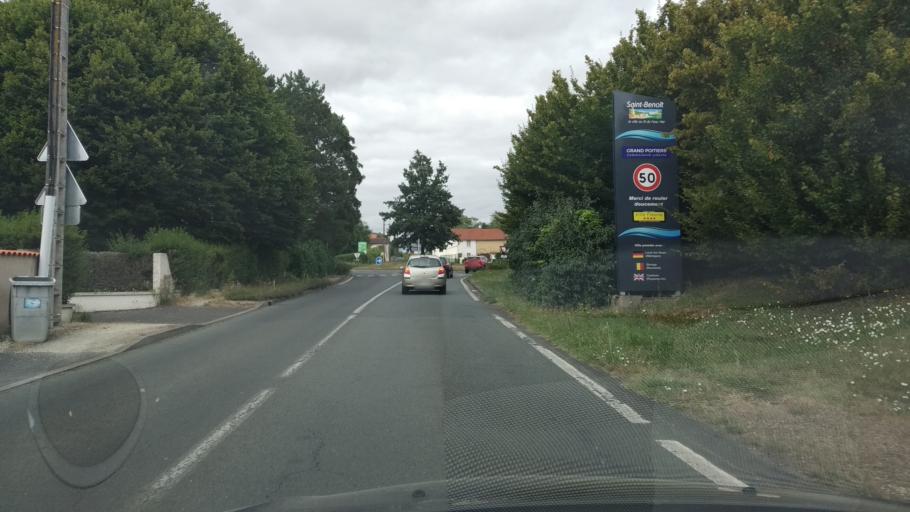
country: FR
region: Poitou-Charentes
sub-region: Departement de la Vienne
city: Saint-Benoit
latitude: 46.5583
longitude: 0.3552
